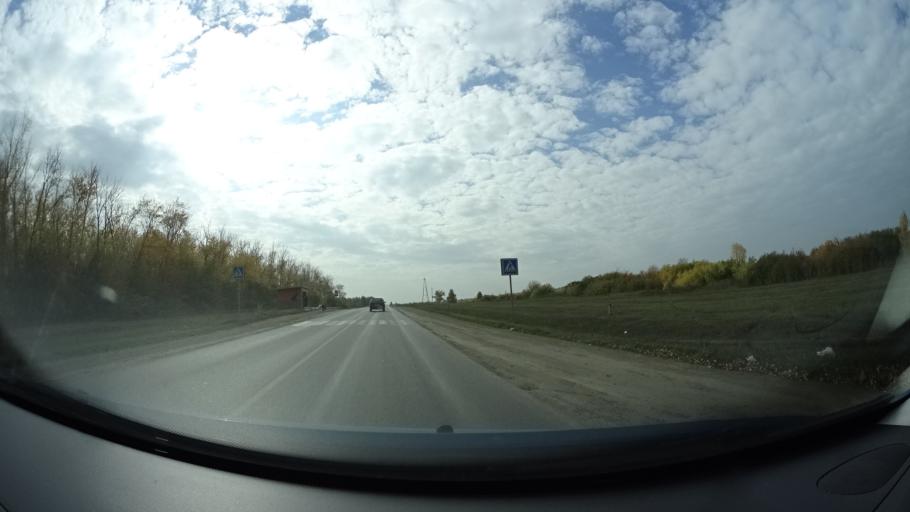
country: RU
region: Bashkortostan
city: Oktyabr'skiy
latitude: 54.5461
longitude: 53.5737
